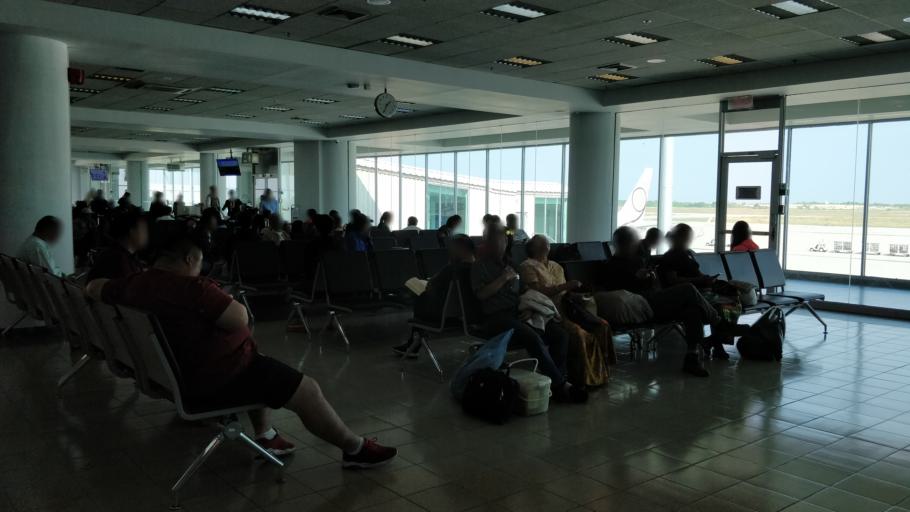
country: MM
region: Sagain
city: Sagaing
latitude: 21.7062
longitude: 95.9705
